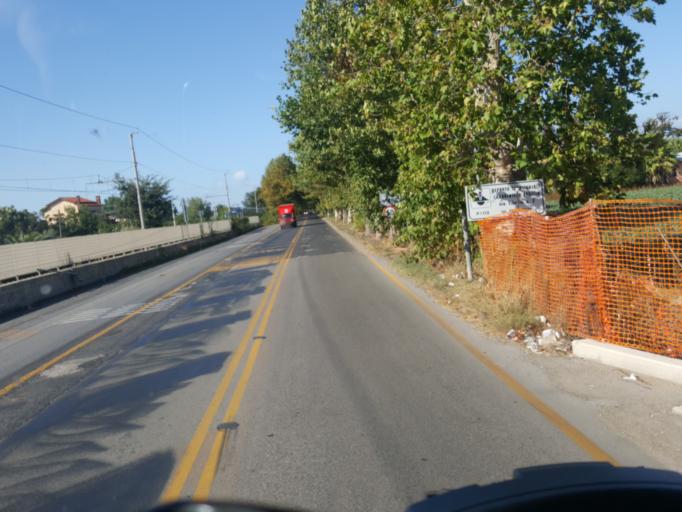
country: IT
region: Latium
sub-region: Provincia di Latina
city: Campo di Carne
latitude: 41.5379
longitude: 12.6345
